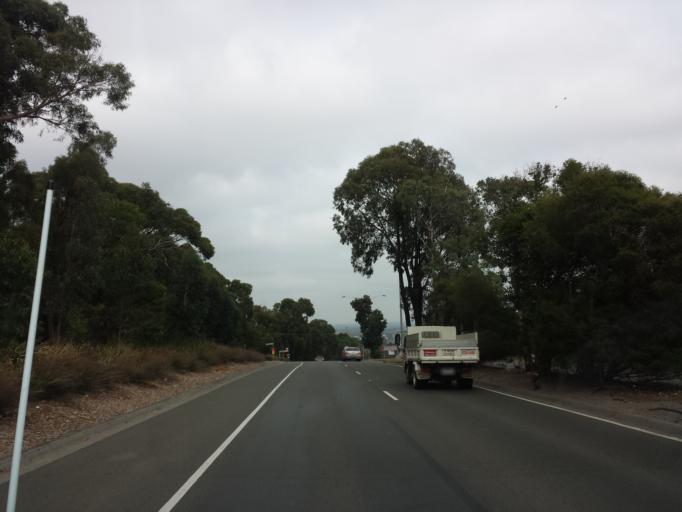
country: AU
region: Victoria
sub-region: Yarra Ranges
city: Montrose
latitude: -37.8135
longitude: 145.3335
